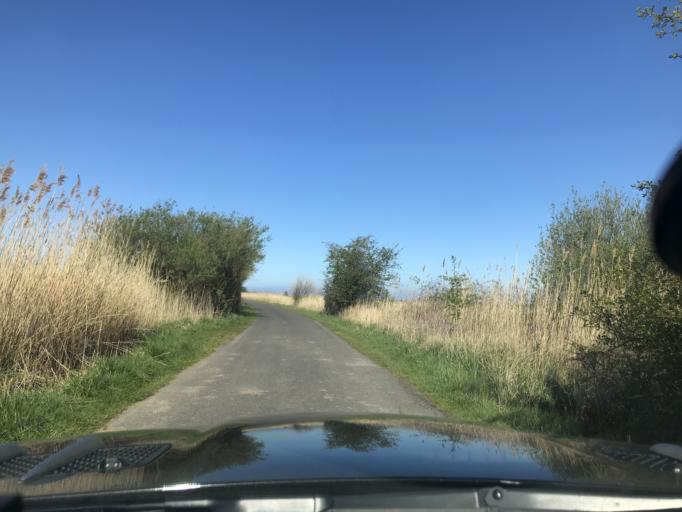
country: DE
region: Schleswig-Holstein
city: Grossenbrode
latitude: 54.4642
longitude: 11.0208
